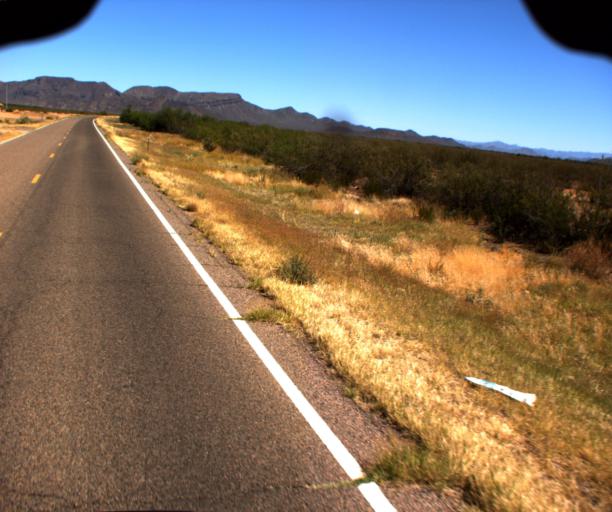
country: US
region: Arizona
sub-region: Yavapai County
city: Congress
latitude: 33.9697
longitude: -113.1415
